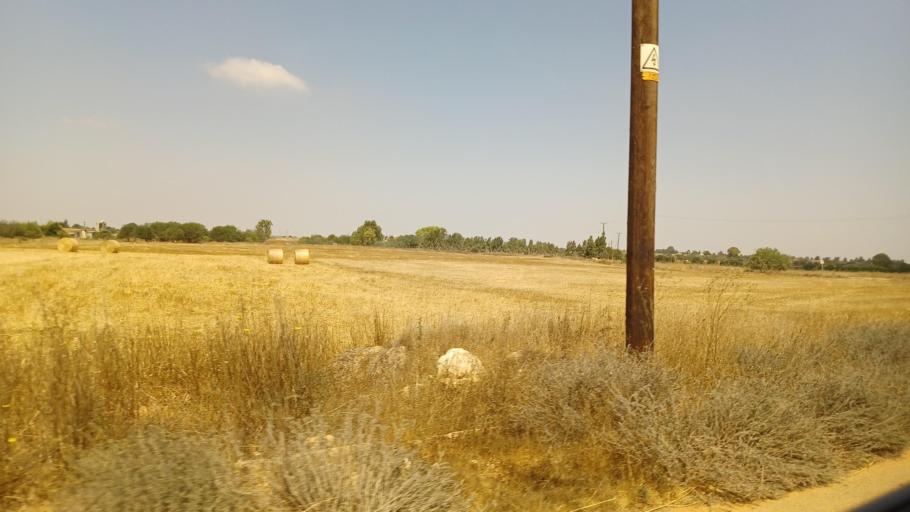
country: CY
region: Ammochostos
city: Frenaros
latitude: 35.0587
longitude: 33.9213
